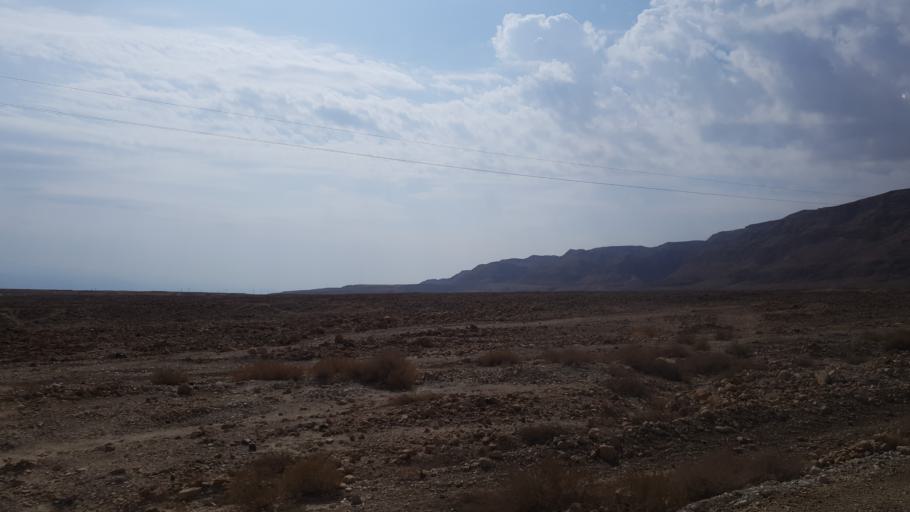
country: IL
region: Southern District
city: `En Boqeq
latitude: 31.3157
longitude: 35.3711
